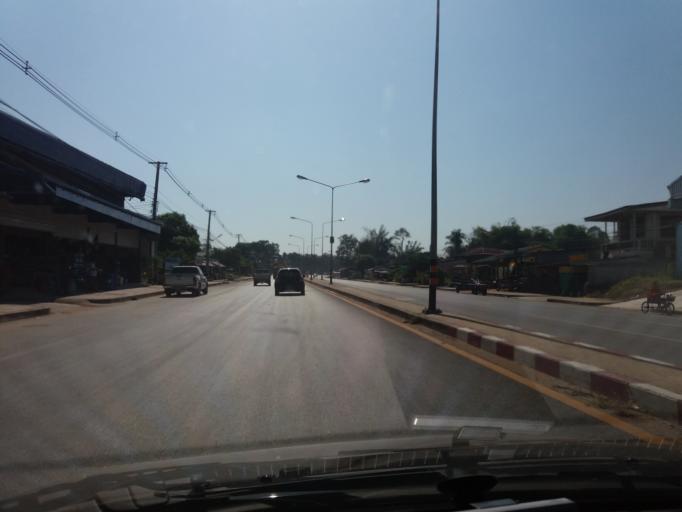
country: TH
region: Kamphaeng Phet
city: Khlong Khlung
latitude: 16.1735
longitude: 99.7962
